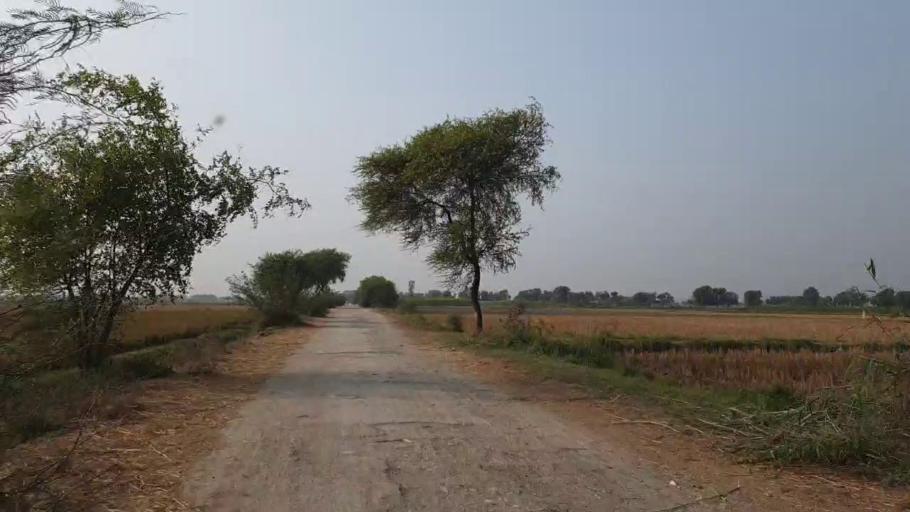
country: PK
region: Sindh
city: Matli
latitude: 25.0690
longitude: 68.5983
